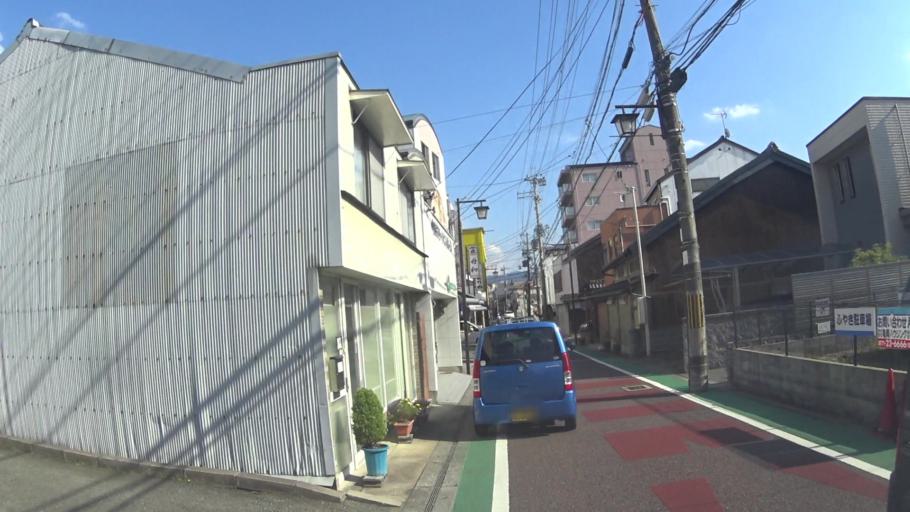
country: JP
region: Kyoto
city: Kameoka
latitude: 35.0165
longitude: 135.5754
